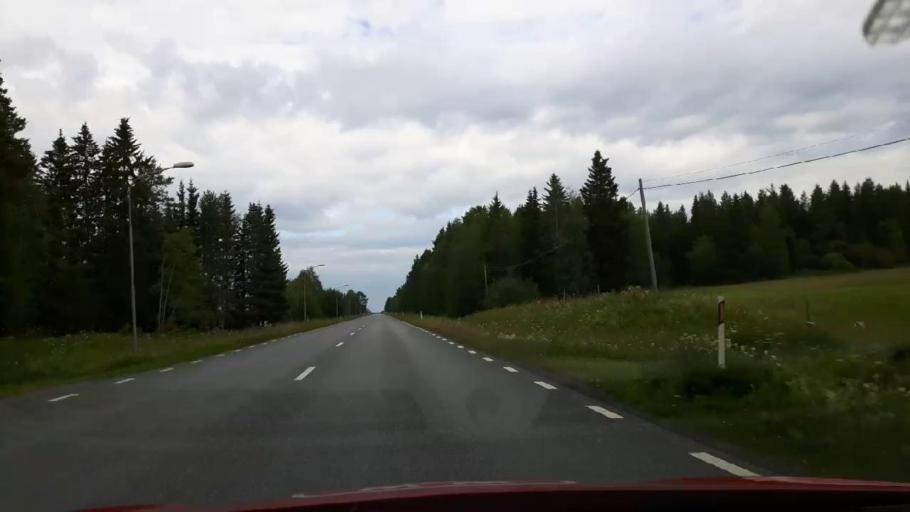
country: SE
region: Jaemtland
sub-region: Stroemsunds Kommun
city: Stroemsund
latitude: 63.5613
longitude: 15.3693
